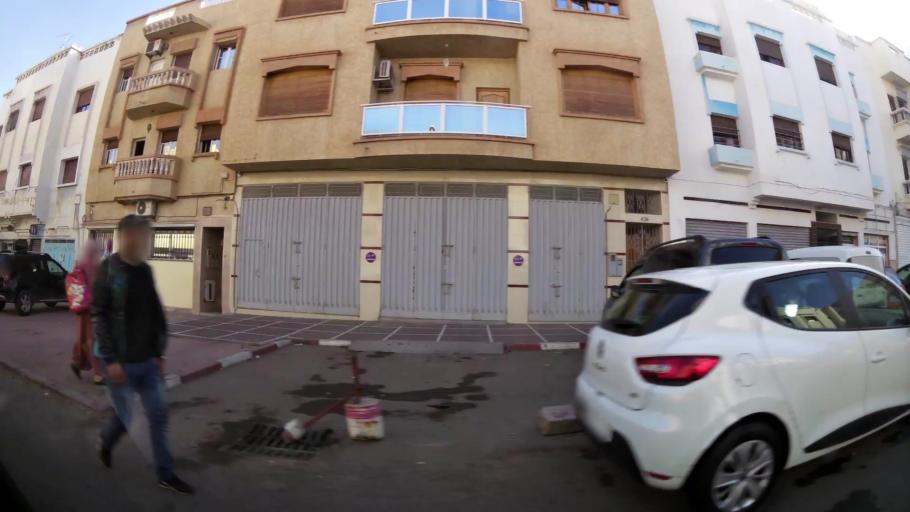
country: MA
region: Oued ed Dahab-Lagouira
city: Dakhla
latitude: 30.4014
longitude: -9.5495
